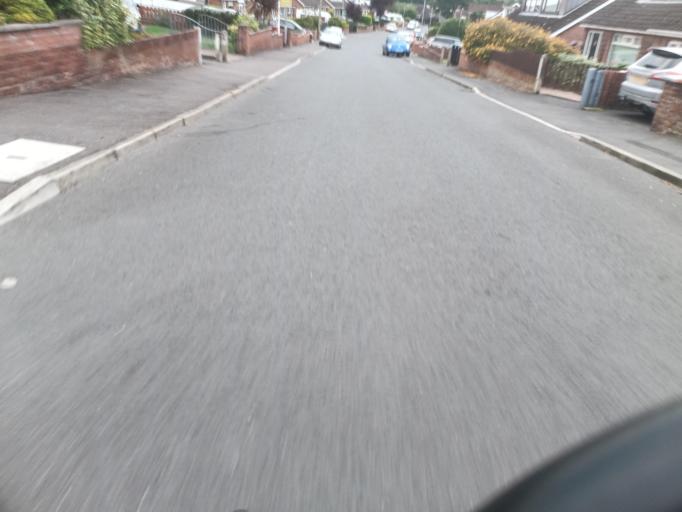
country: GB
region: Northern Ireland
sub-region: Ards District
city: Comber
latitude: 54.5543
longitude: -5.7311
